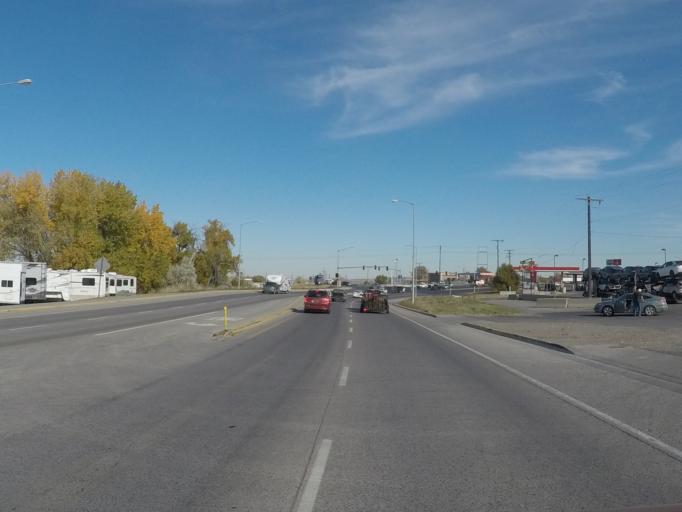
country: US
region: Montana
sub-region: Yellowstone County
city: Billings
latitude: 45.7964
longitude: -108.4626
